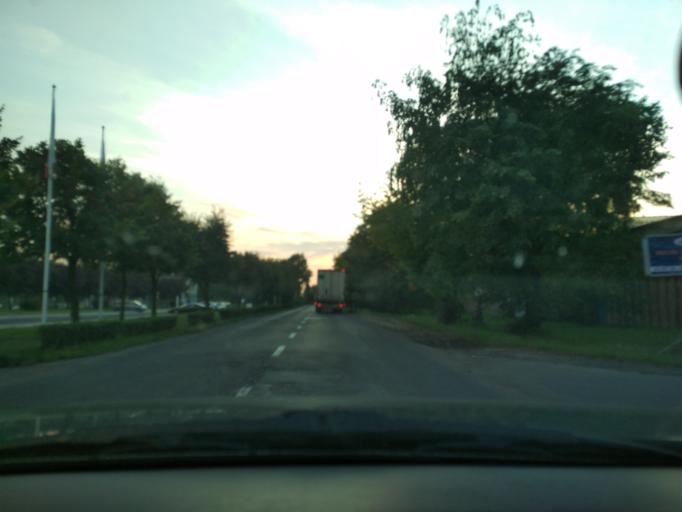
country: PL
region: Silesian Voivodeship
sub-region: Gliwice
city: Gliwice
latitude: 50.2665
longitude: 18.7049
